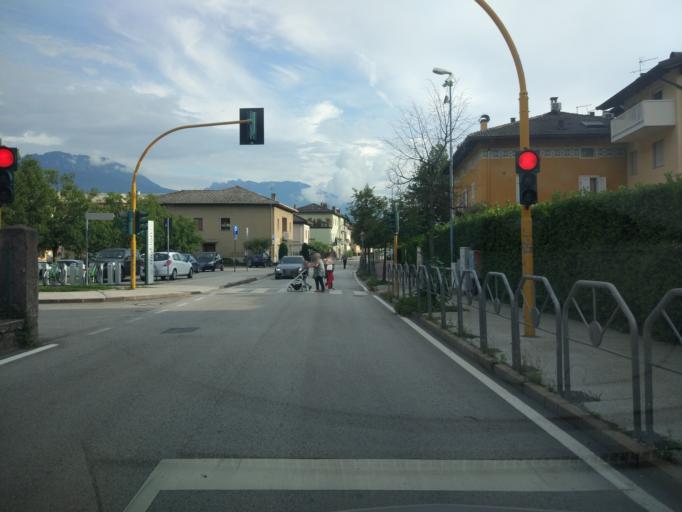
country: IT
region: Trentino-Alto Adige
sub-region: Provincia di Trento
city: Meano
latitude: 46.1047
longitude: 11.1128
